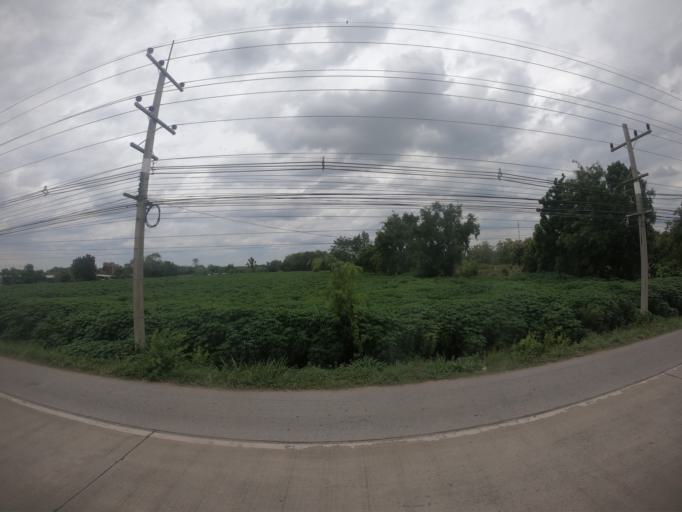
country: TH
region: Nakhon Ratchasima
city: Chok Chai
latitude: 14.7984
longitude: 102.1706
